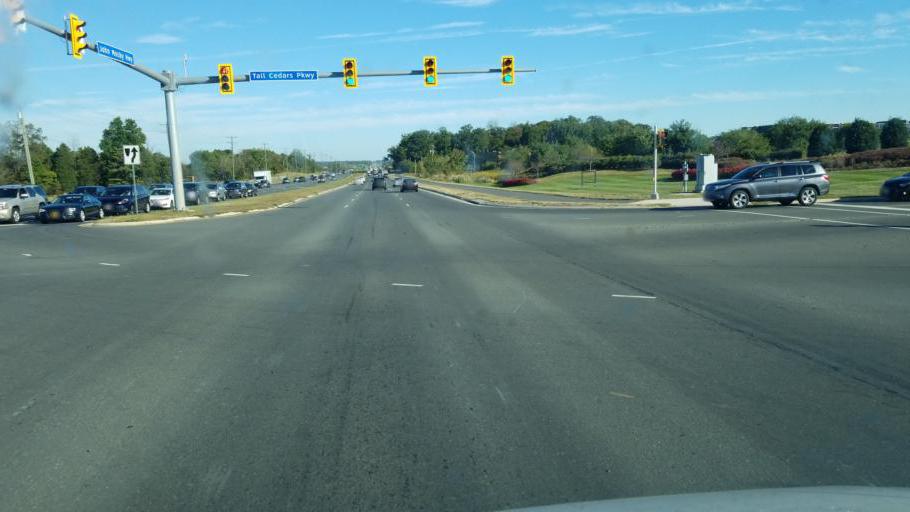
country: US
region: Virginia
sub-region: Loudoun County
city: South Riding
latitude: 38.9163
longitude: -77.4862
